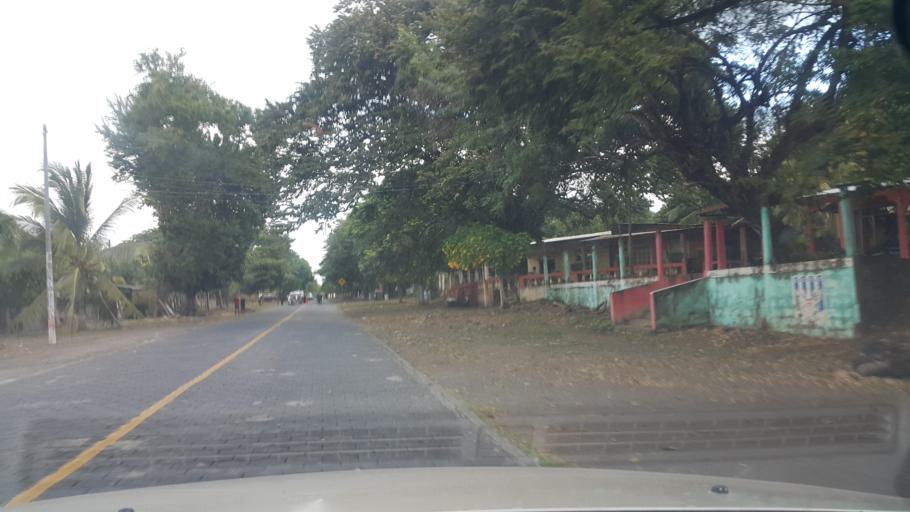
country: NI
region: Rivas
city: Moyogalpa
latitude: 11.5304
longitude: -85.6994
